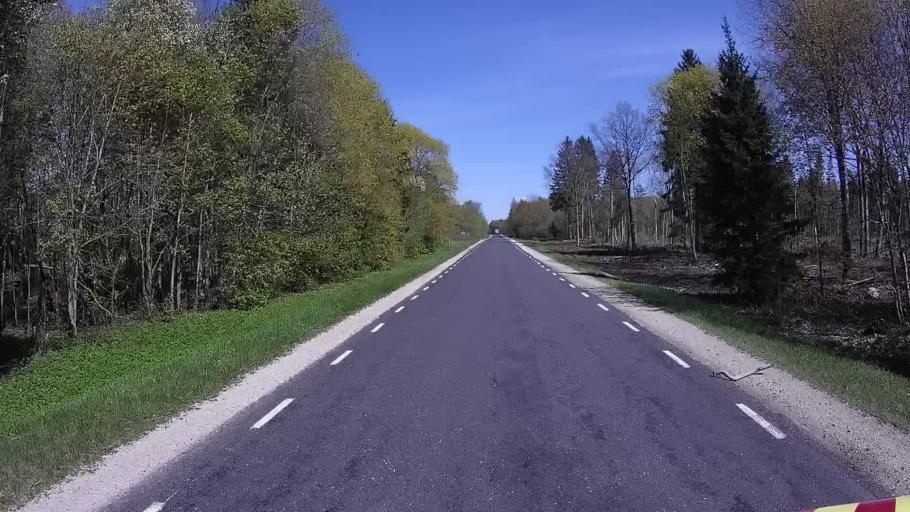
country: EE
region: Laeaene
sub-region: Ridala Parish
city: Uuemoisa
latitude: 59.0170
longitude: 23.7939
